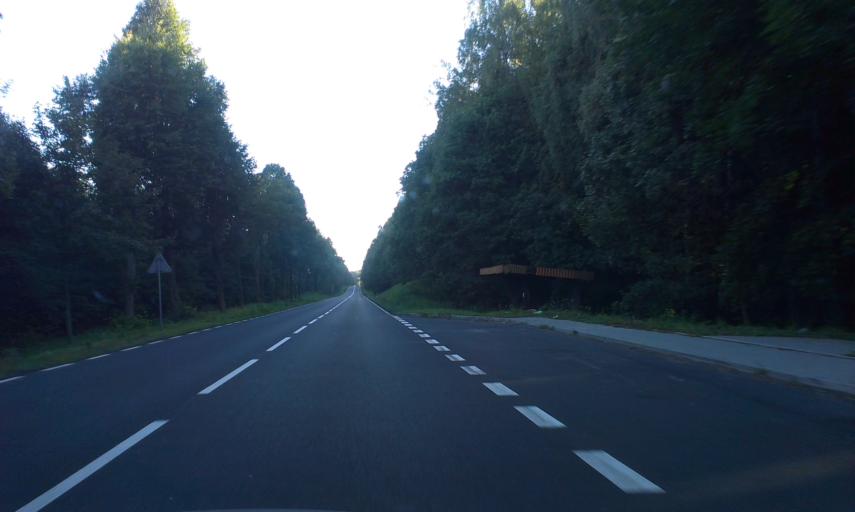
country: PL
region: West Pomeranian Voivodeship
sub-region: Powiat szczecinecki
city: Szczecinek
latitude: 53.8014
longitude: 16.6401
